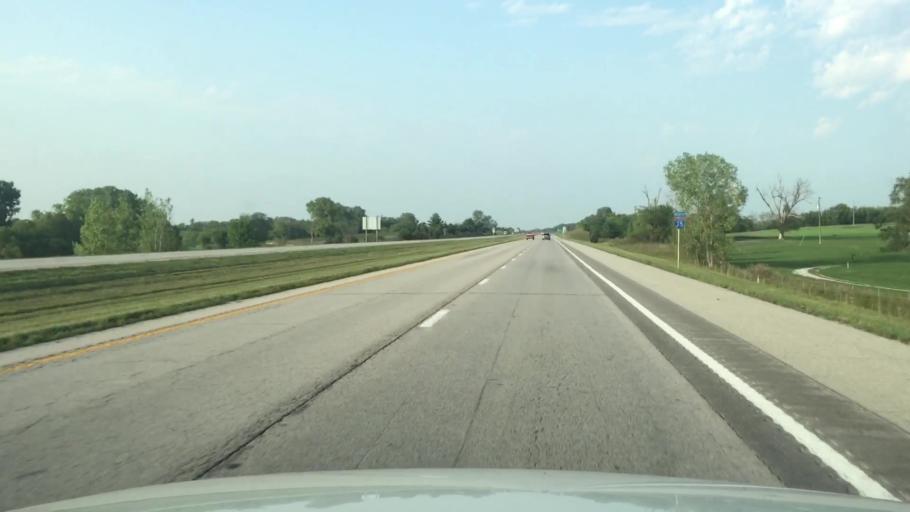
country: US
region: Missouri
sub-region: Harrison County
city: Bethany
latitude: 40.1605
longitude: -94.0287
